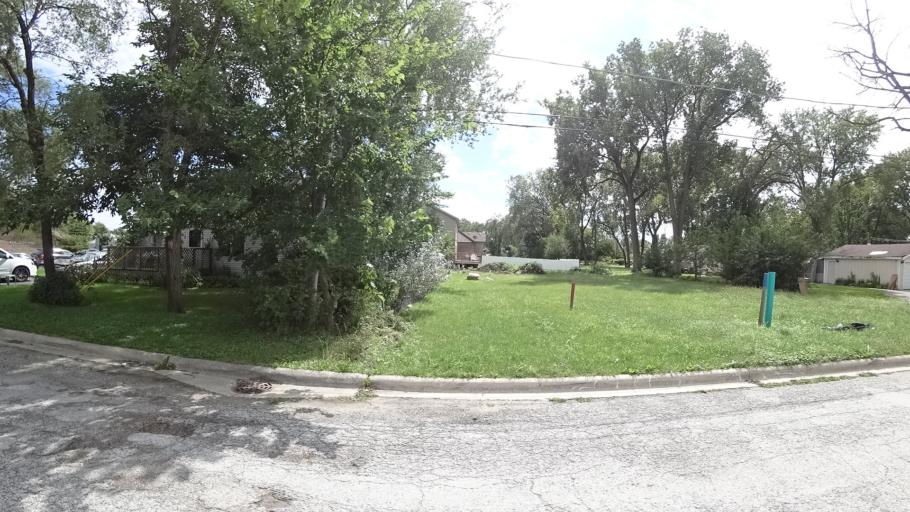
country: US
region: Illinois
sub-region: Cook County
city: Chicago Ridge
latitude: 41.7139
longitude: -87.7899
